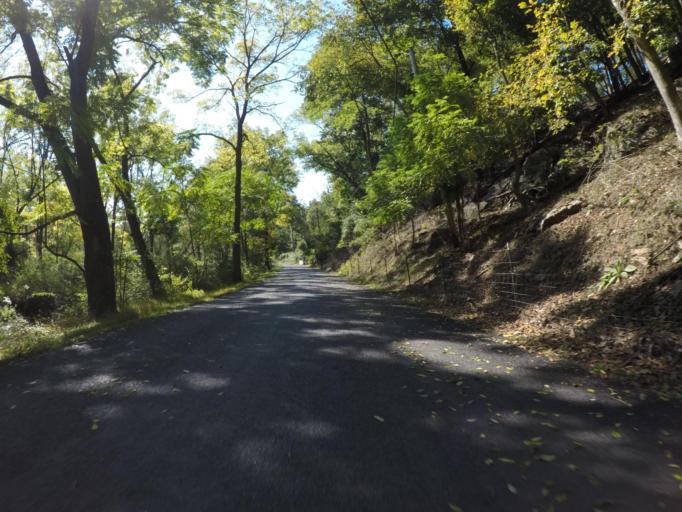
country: US
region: Maryland
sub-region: Carroll County
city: Hampstead
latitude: 39.5883
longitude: -76.8866
